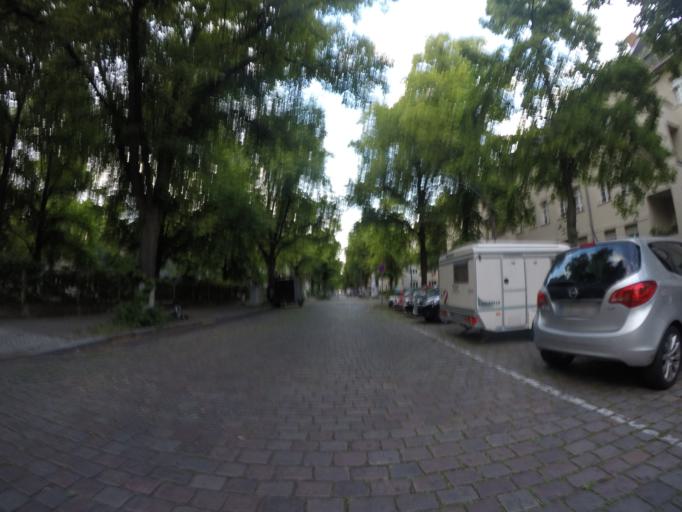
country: DE
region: Berlin
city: Schmargendorf
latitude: 52.4786
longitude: 13.2887
